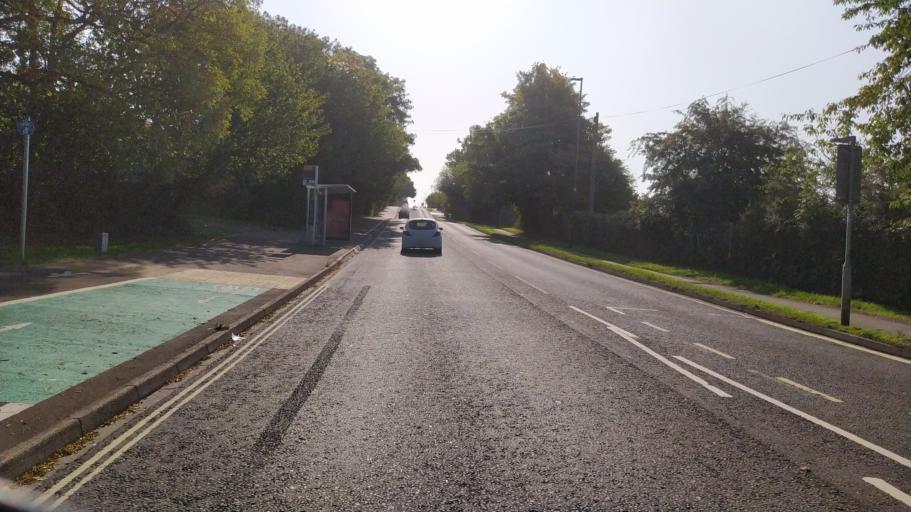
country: GB
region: England
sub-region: Hampshire
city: West End
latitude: 50.9104
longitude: -1.3499
